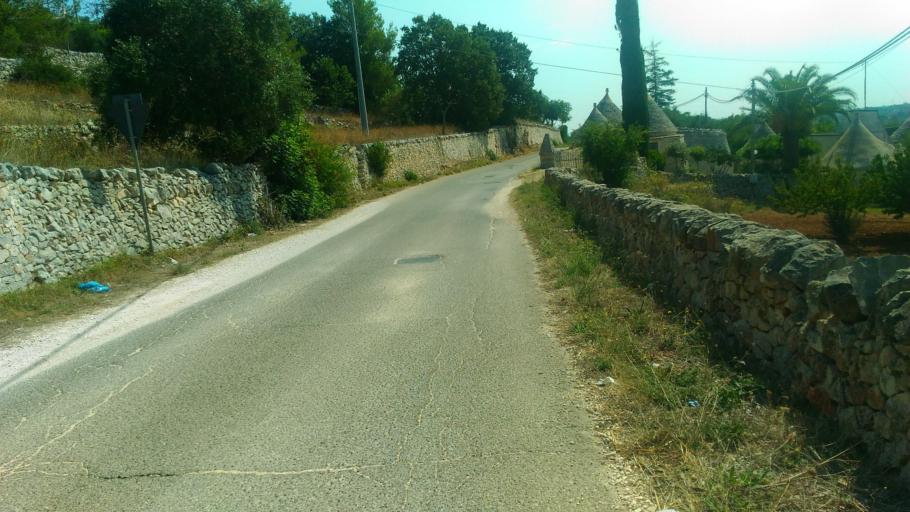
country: IT
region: Apulia
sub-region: Provincia di Bari
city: Locorotondo
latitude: 40.7520
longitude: 17.3410
